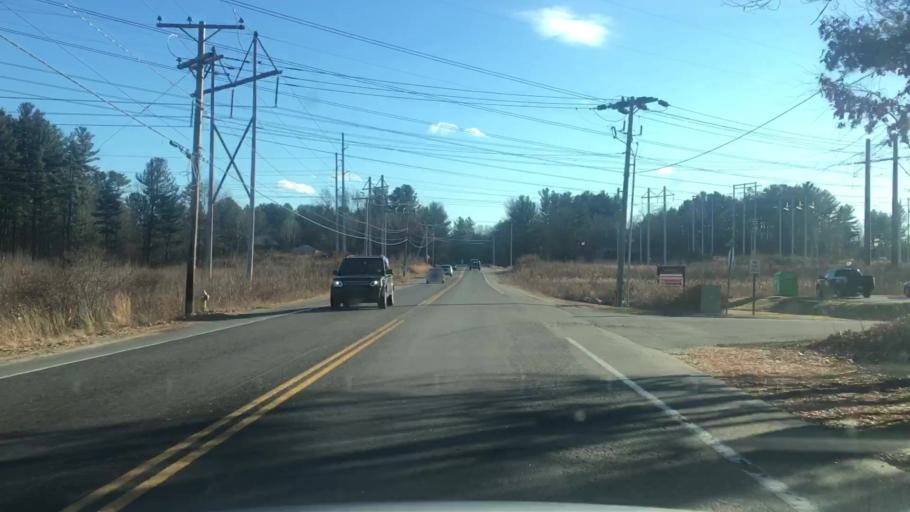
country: US
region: New Hampshire
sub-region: Rockingham County
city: Londonderry
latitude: 42.8818
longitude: -71.3817
